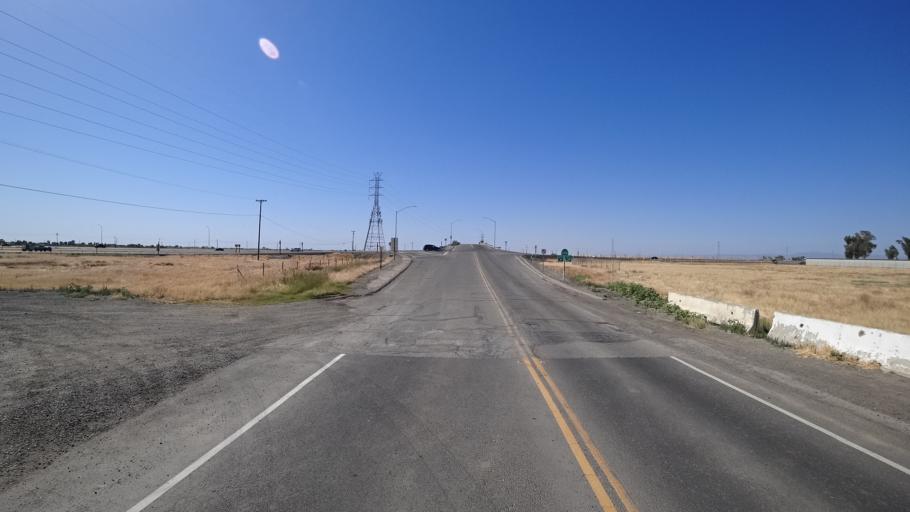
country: US
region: California
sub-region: Kings County
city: Lemoore Station
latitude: 36.2572
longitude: -119.8695
